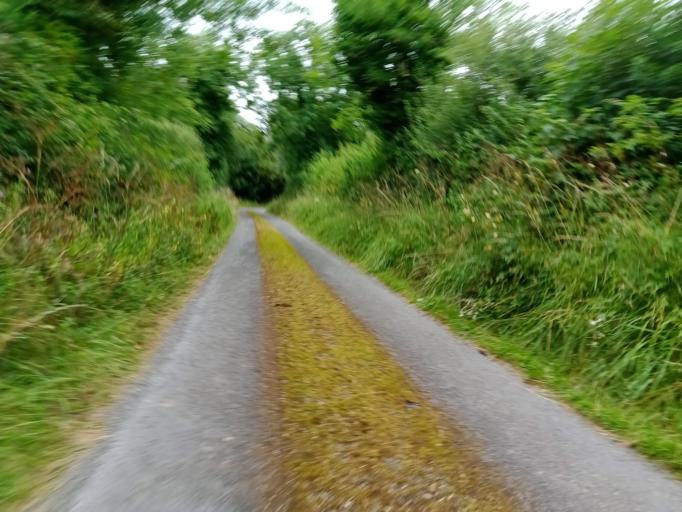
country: IE
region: Leinster
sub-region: Kilkenny
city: Callan
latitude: 52.5354
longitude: -7.4218
